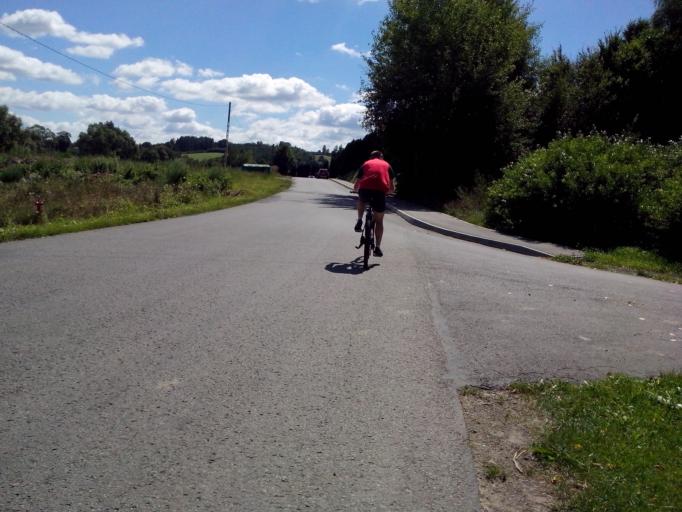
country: PL
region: Subcarpathian Voivodeship
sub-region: Powiat brzozowski
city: Golcowa
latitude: 49.7762
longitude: 21.9994
